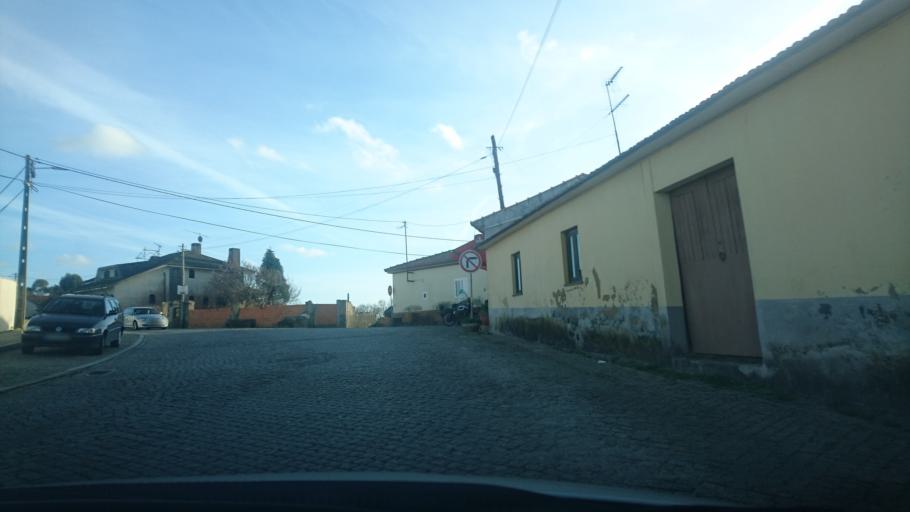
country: PT
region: Aveiro
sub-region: Santa Maria da Feira
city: Pacos de Brandao
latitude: 40.9857
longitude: -8.5965
